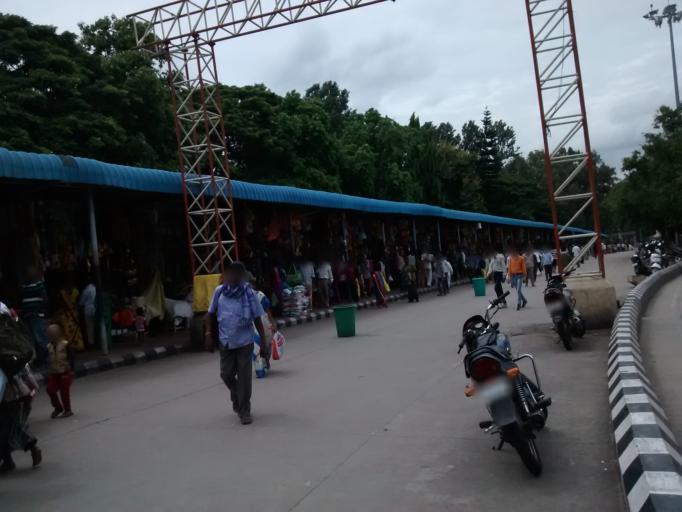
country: IN
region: Andhra Pradesh
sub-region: Chittoor
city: Tirumala
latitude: 13.6781
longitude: 79.3506
